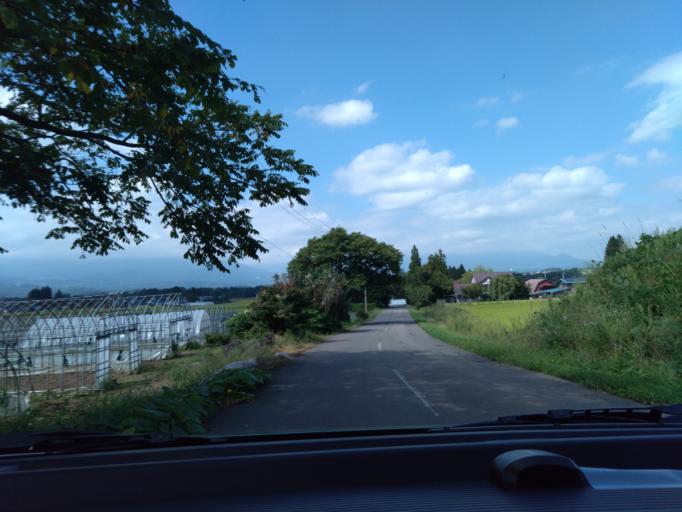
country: JP
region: Iwate
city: Shizukuishi
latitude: 39.6803
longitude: 140.9591
